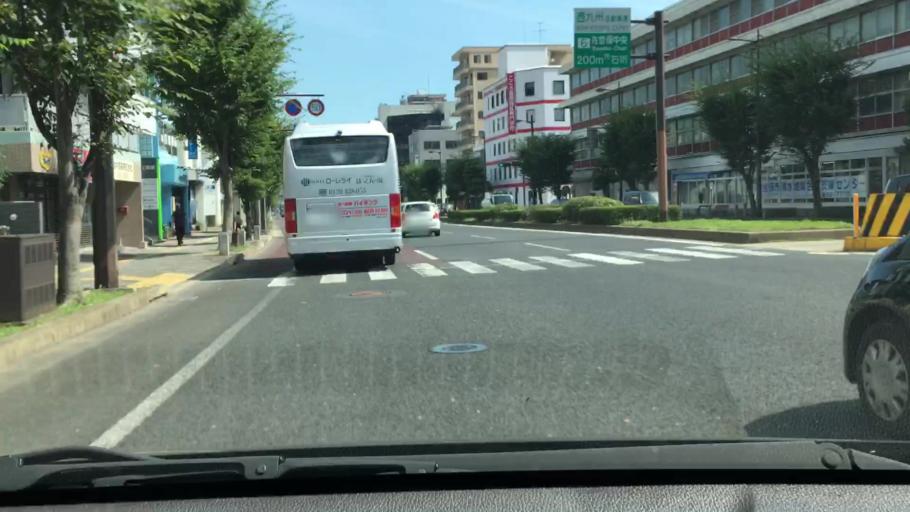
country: JP
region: Nagasaki
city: Sasebo
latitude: 33.1776
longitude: 129.7169
